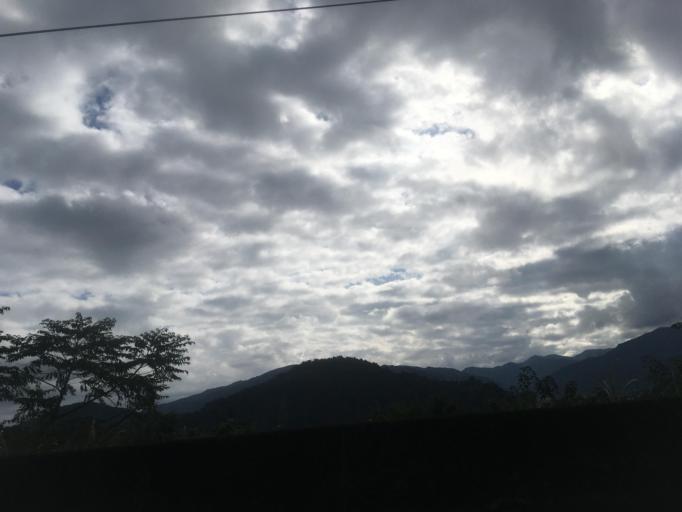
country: TW
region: Taiwan
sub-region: Yilan
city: Yilan
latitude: 24.6589
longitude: 121.5871
